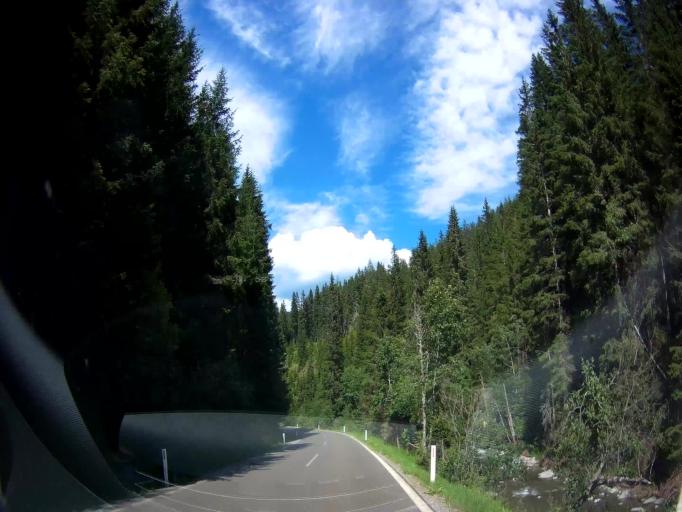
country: AT
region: Styria
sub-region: Politischer Bezirk Murau
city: Stadl an der Mur
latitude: 47.0216
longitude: 14.0053
